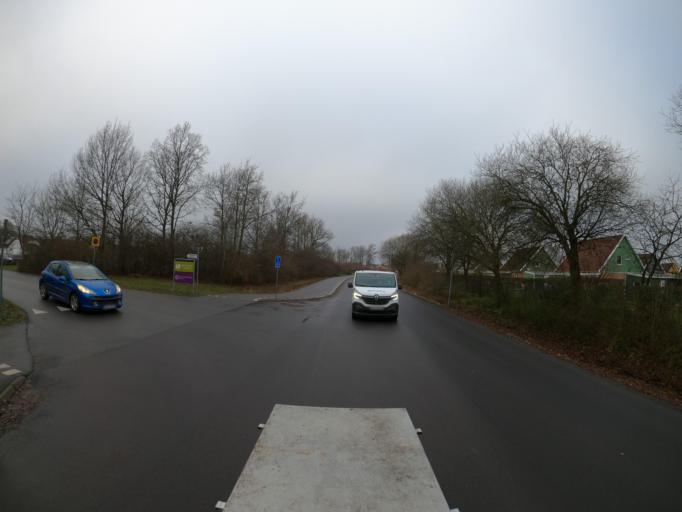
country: SE
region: Skane
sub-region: Svedala Kommun
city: Svedala
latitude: 55.5182
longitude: 13.2328
